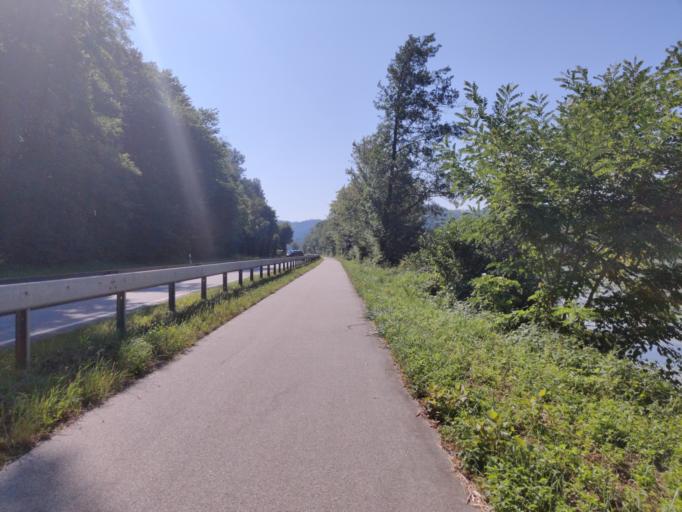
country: DE
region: Bavaria
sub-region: Lower Bavaria
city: Thyrnau
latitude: 48.5754
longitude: 13.5458
